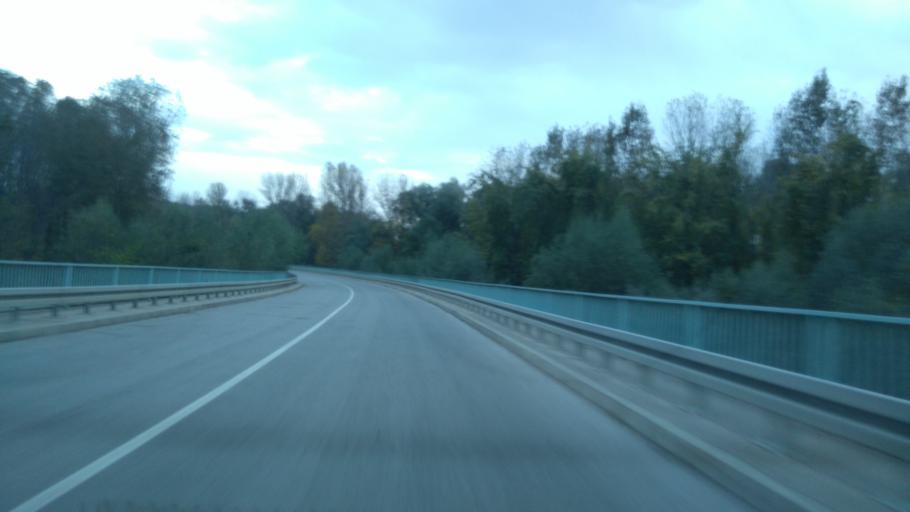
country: RS
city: Mol
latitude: 45.7845
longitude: 20.1497
